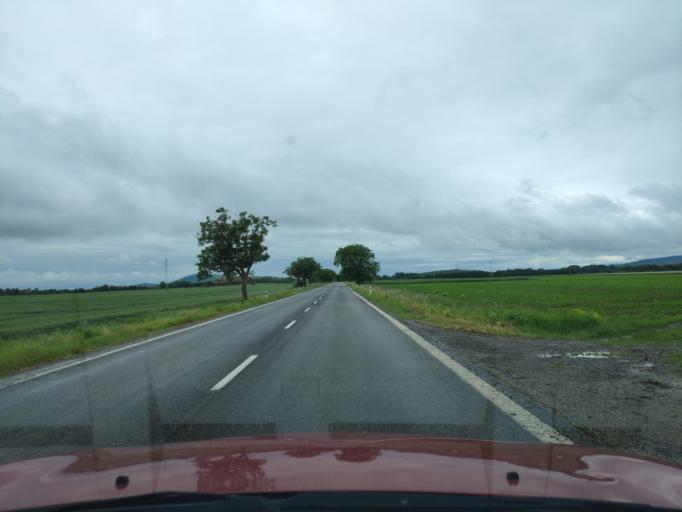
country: HU
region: Borsod-Abauj-Zemplen
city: Karcsa
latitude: 48.4264
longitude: 21.8437
